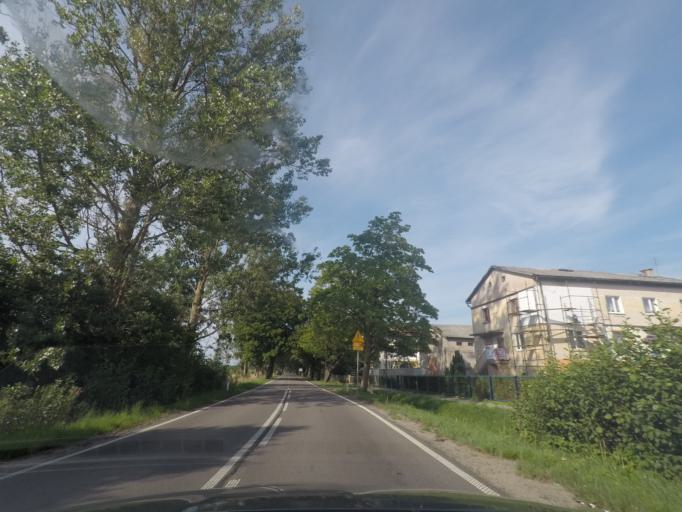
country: PL
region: Pomeranian Voivodeship
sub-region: Powiat leborski
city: Leba
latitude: 54.6457
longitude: 17.5520
